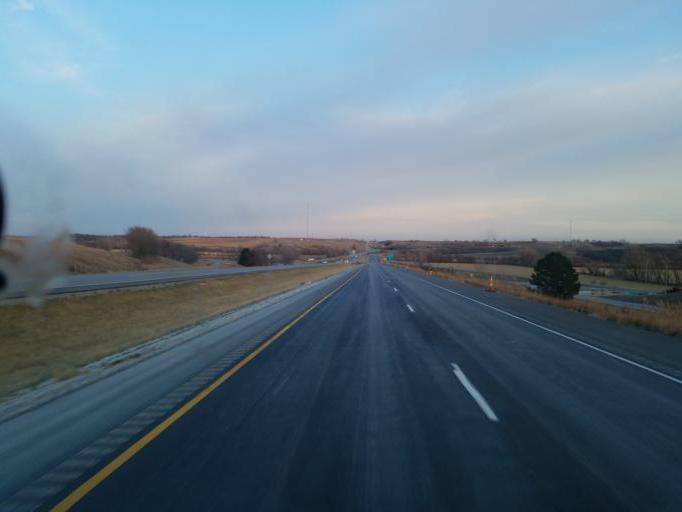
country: US
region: Iowa
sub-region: Harrison County
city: Logan
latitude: 41.4988
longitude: -95.6048
